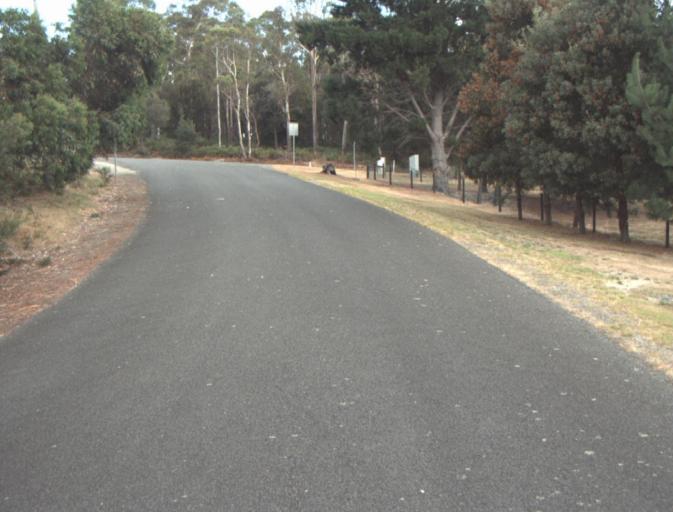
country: AU
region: Tasmania
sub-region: Launceston
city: Mayfield
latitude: -41.2819
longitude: 147.0197
